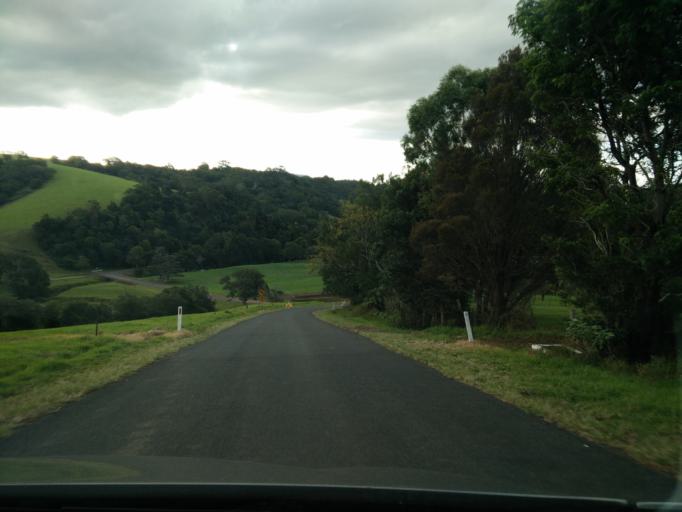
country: AU
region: New South Wales
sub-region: Kiama
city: Jamberoo
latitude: -34.6694
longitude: 150.7919
